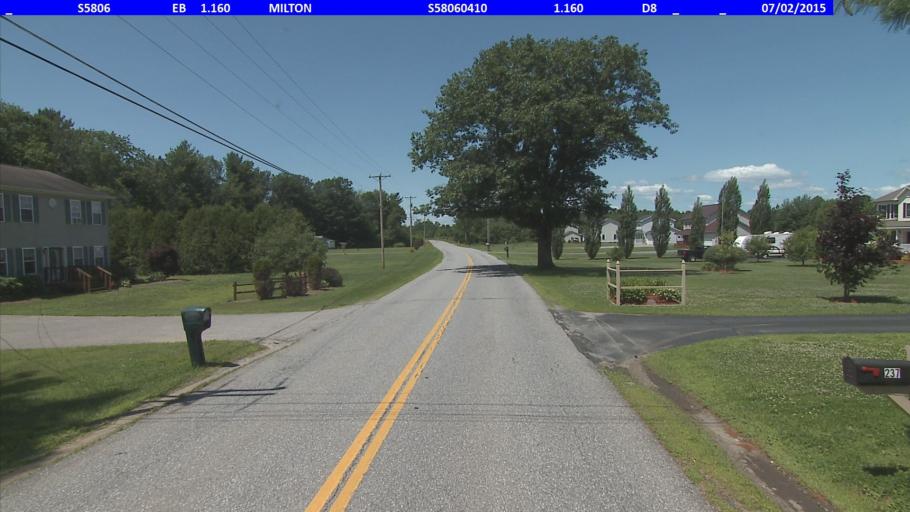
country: US
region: Vermont
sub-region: Chittenden County
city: Milton
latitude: 44.6601
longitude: -73.1335
